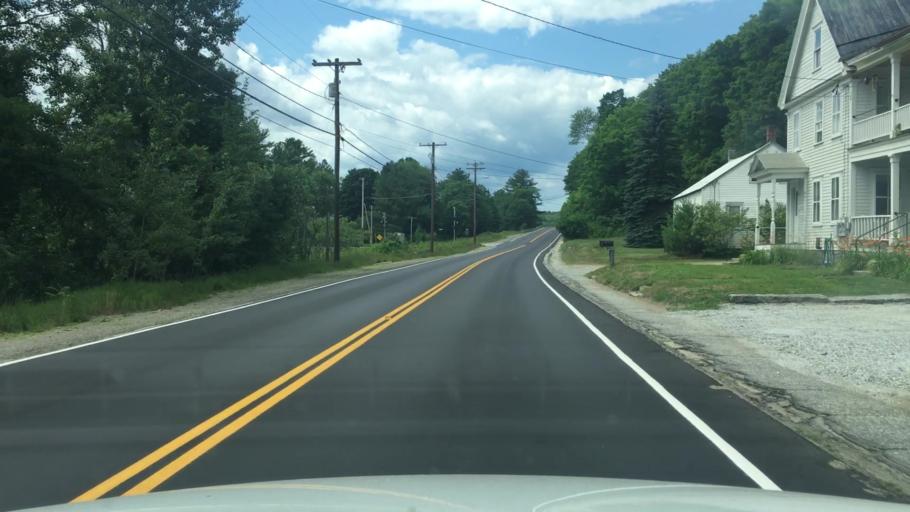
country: US
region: Maine
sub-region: Oxford County
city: West Paris
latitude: 44.3805
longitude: -70.6488
